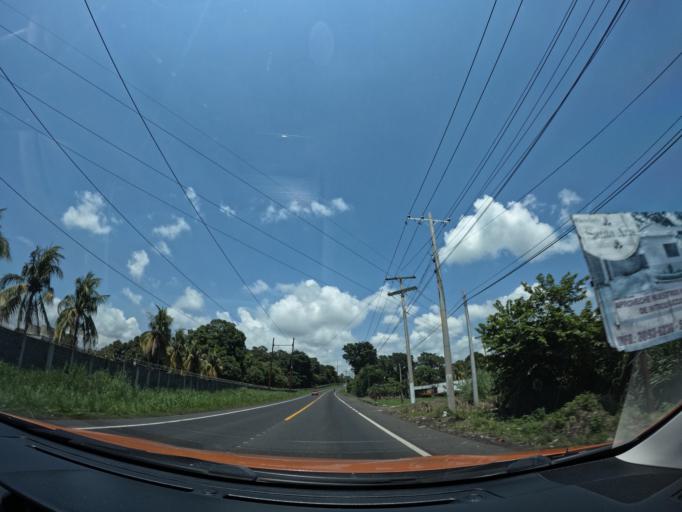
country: GT
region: Escuintla
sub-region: Municipio de Escuintla
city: Escuintla
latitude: 14.2642
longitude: -90.7960
